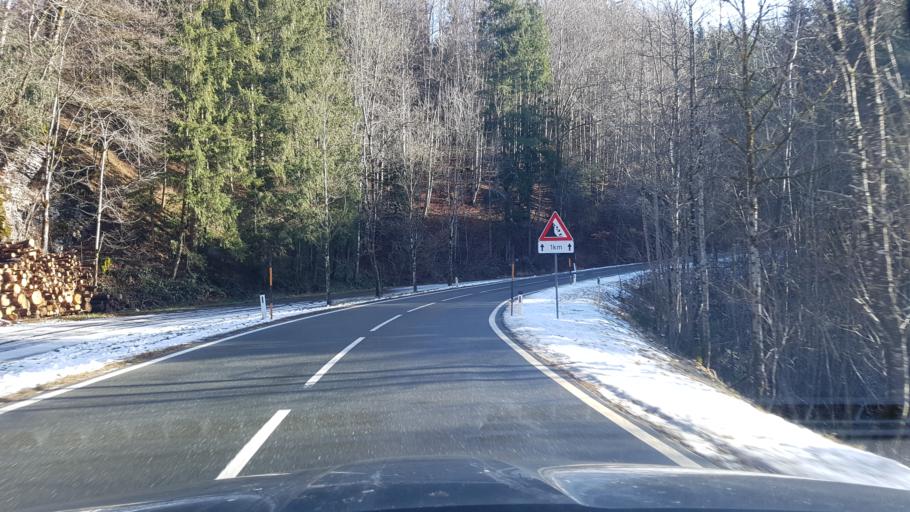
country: AT
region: Salzburg
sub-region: Politischer Bezirk Hallein
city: Krispl
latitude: 47.7229
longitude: 13.1885
